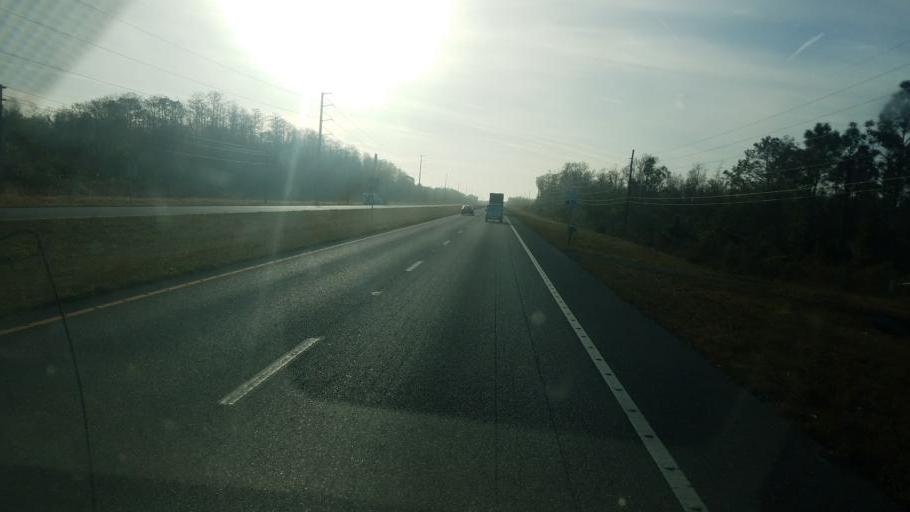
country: US
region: Florida
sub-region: Osceola County
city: Saint Cloud
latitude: 28.1662
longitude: -81.1238
